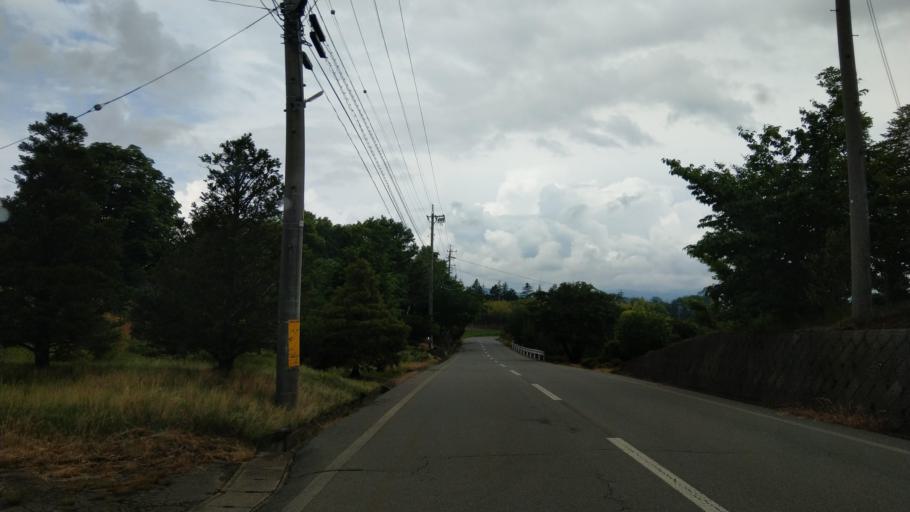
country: JP
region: Nagano
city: Komoro
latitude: 36.2989
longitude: 138.3812
